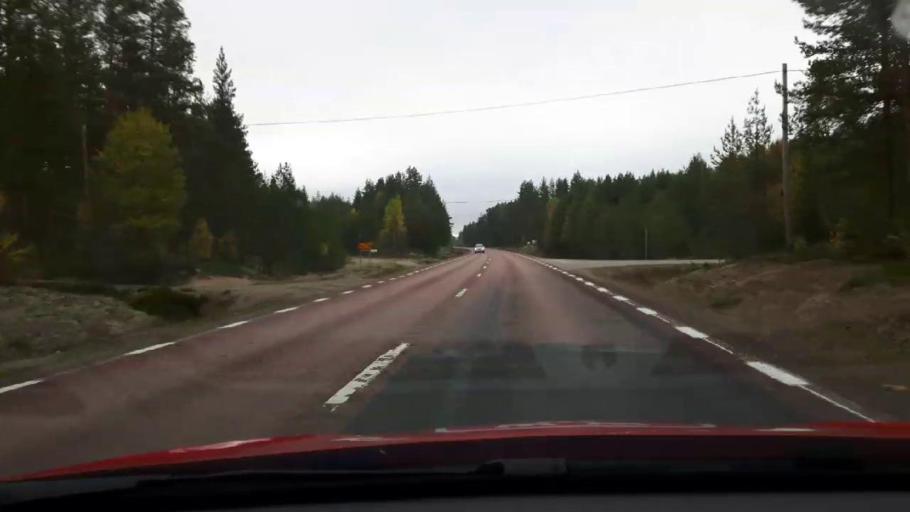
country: SE
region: Gaevleborg
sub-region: Ljusdals Kommun
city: Farila
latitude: 61.8329
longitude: 15.7509
